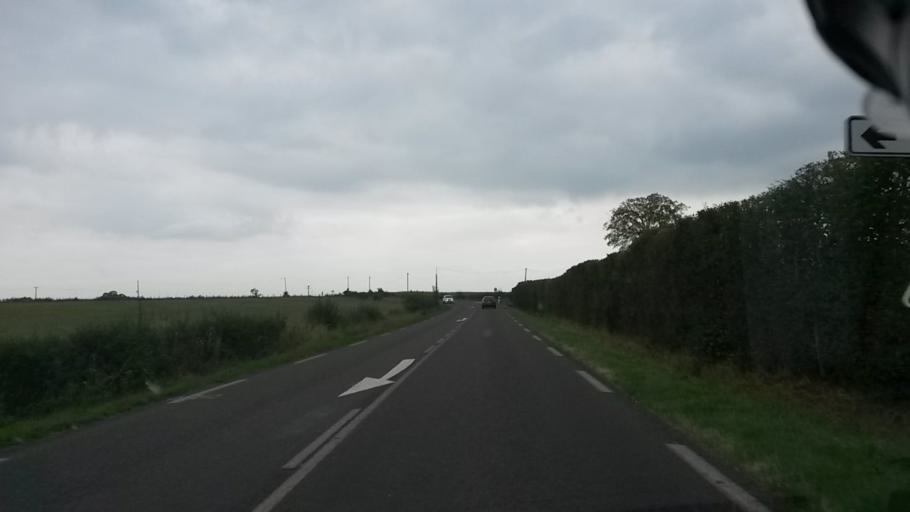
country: FR
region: Haute-Normandie
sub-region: Departement de la Seine-Maritime
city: Gaillefontaine
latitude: 49.6386
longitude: 1.6084
